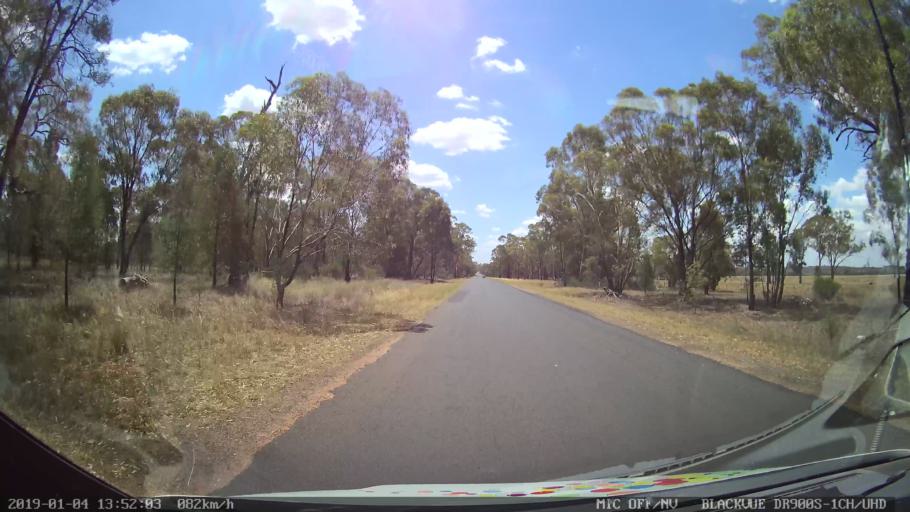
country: AU
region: New South Wales
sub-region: Dubbo Municipality
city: Dubbo
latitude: -32.3992
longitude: 148.5713
